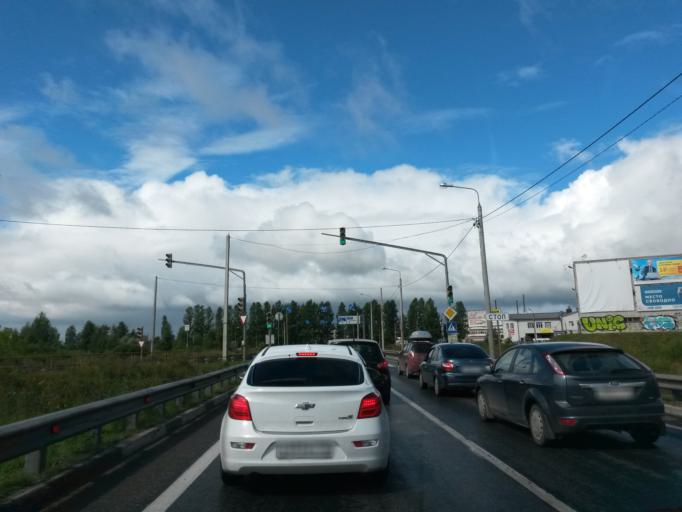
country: RU
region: Jaroslavl
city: Yaroslavl
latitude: 57.6714
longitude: 39.7753
